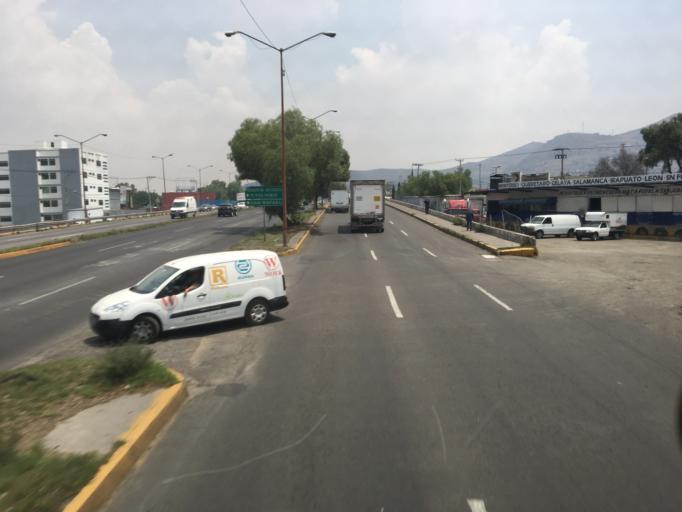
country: MX
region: Mexico
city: Tlalnepantla
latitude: 19.5449
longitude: -99.1827
